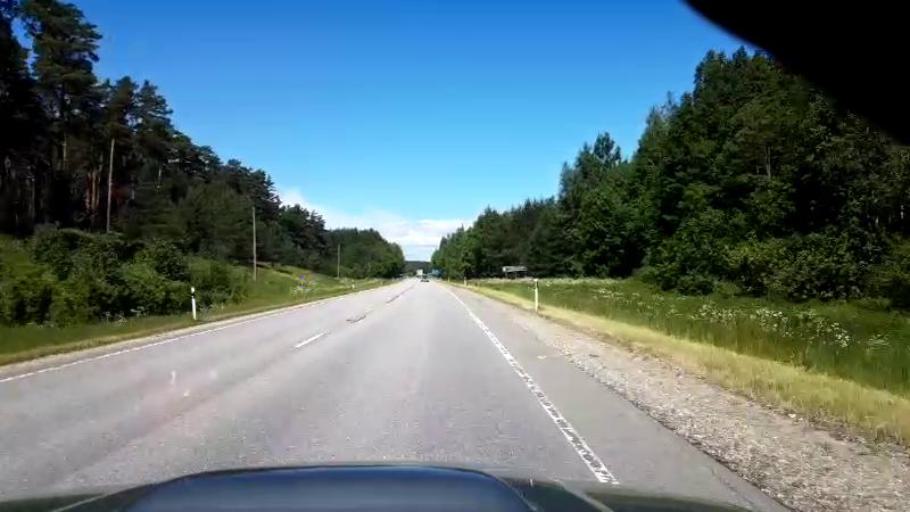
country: LV
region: Salacgrivas
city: Ainazi
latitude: 58.0833
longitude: 24.5098
